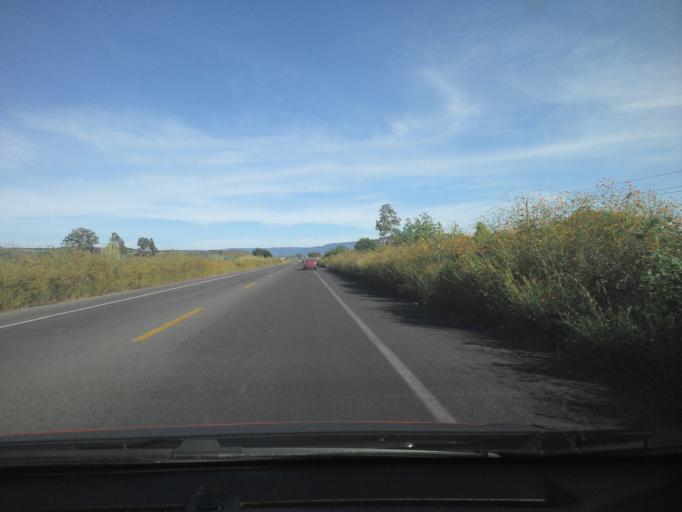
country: MX
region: Jalisco
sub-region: Teuchitlan
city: La Estanzuela
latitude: 20.6709
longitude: -103.8113
